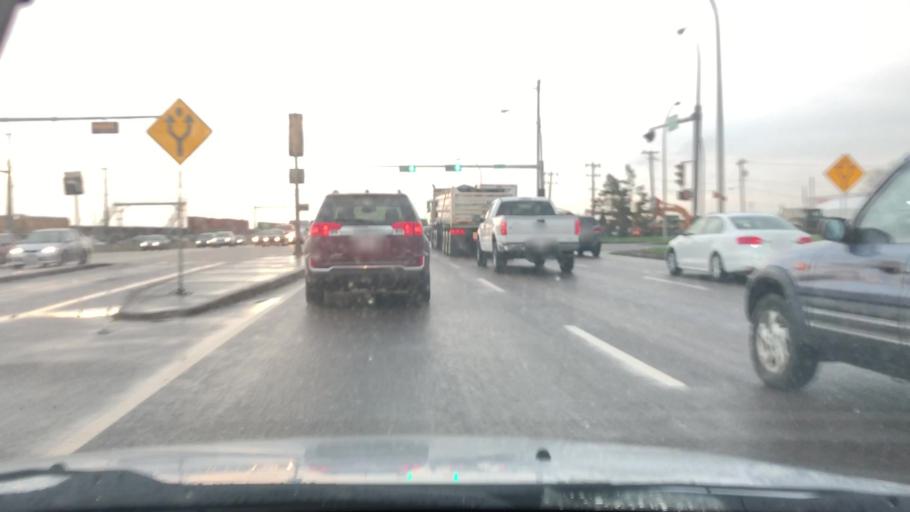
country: CA
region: Alberta
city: Edmonton
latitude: 53.5807
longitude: -113.5264
